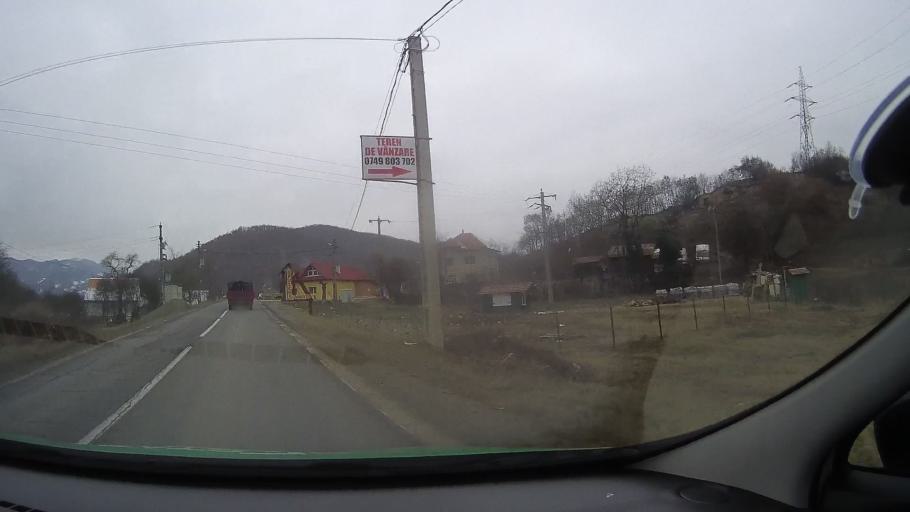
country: RO
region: Alba
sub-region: Comuna Ighiu
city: Ighiel
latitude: 46.1117
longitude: 23.4891
